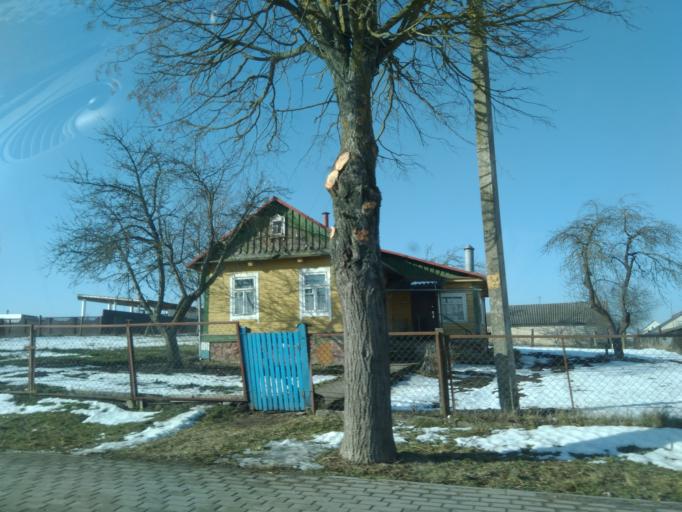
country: BY
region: Minsk
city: Nyasvizh
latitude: 53.2108
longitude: 26.6647
